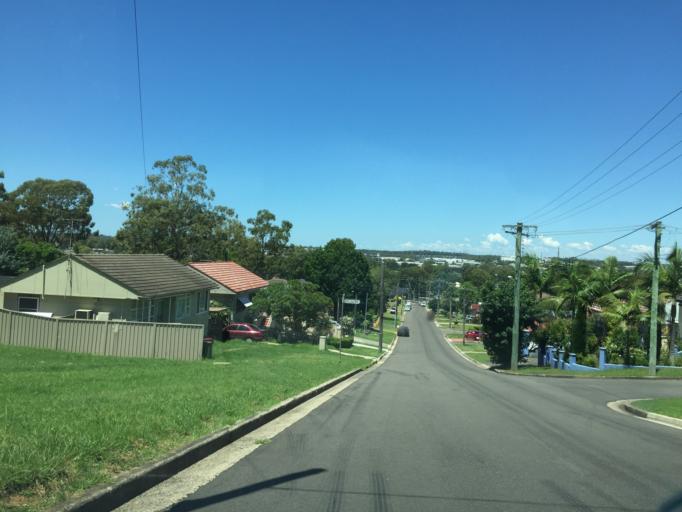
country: AU
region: New South Wales
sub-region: Blacktown
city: Doonside
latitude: -33.7790
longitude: 150.8869
